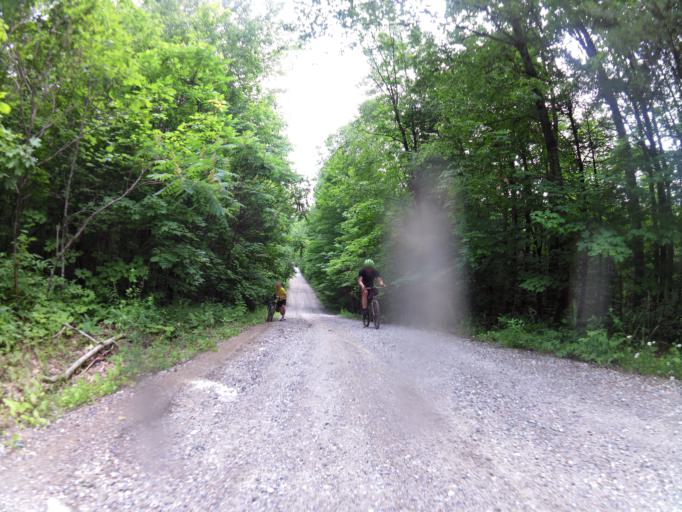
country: CA
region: Ontario
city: Perth
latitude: 45.0108
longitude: -76.5954
